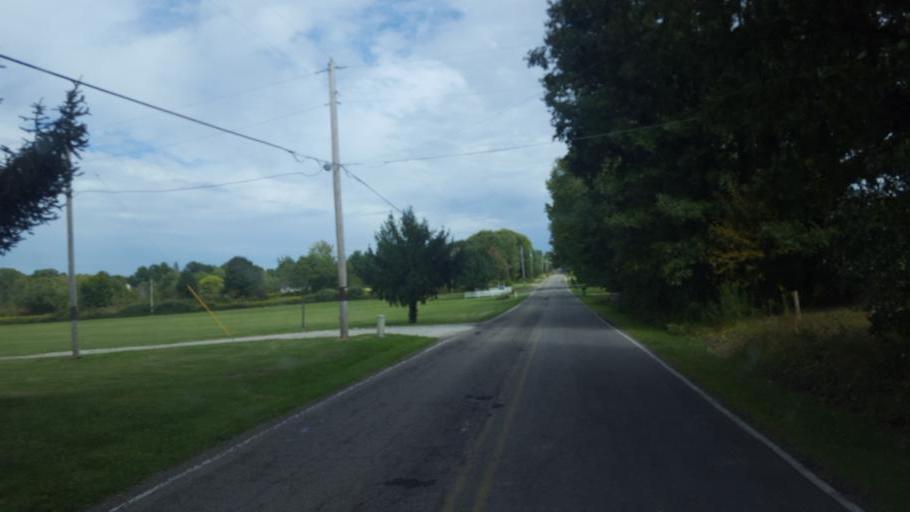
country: US
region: Ohio
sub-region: Licking County
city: Johnstown
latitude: 40.0957
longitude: -82.7201
